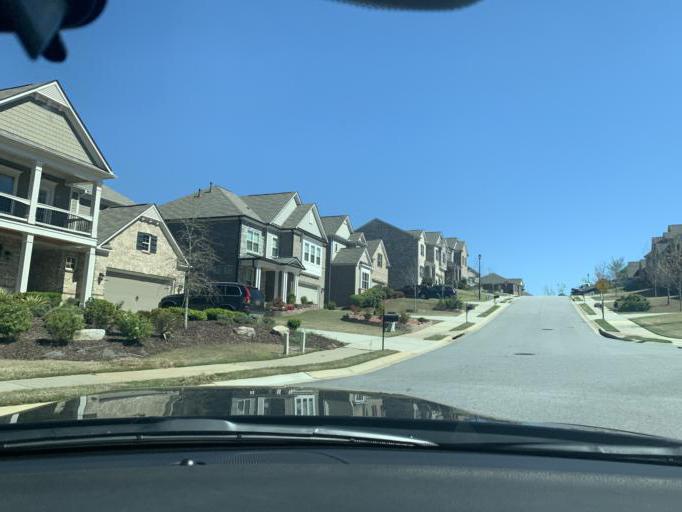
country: US
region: Georgia
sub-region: Fulton County
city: Johns Creek
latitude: 34.1221
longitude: -84.2059
